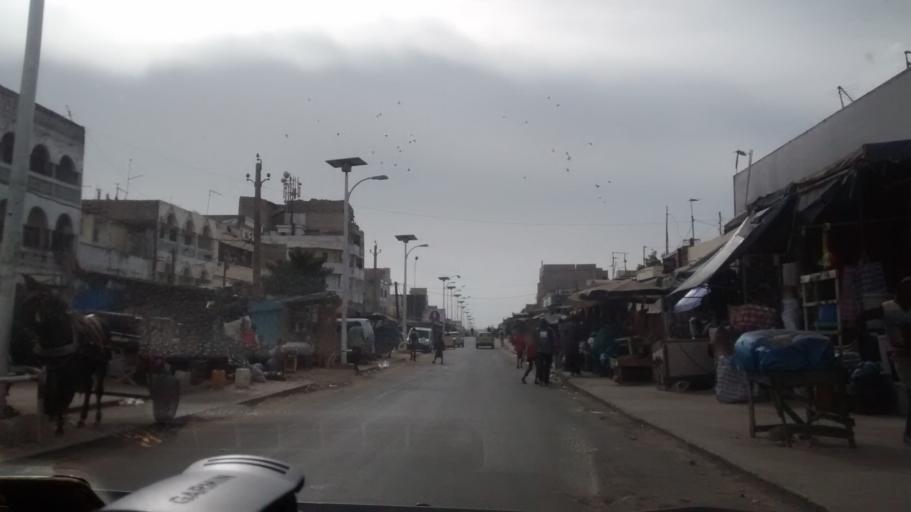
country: SN
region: Dakar
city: Pikine
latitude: 14.7801
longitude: -17.3805
